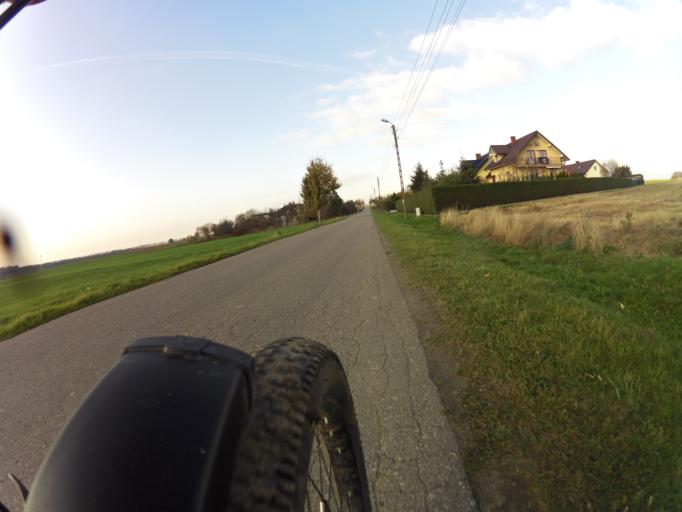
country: PL
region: Pomeranian Voivodeship
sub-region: Powiat pucki
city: Krokowa
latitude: 54.7595
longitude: 18.1830
